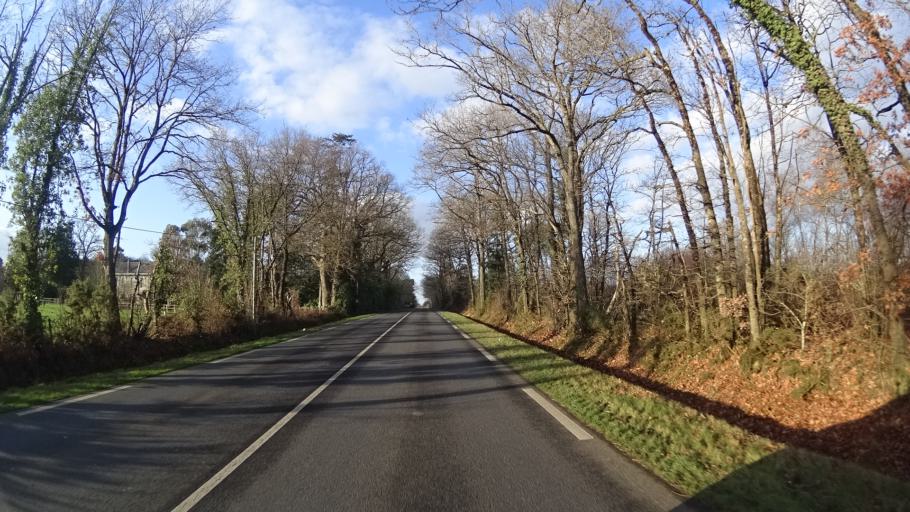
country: FR
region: Pays de la Loire
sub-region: Departement de la Loire-Atlantique
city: Saint-Nicolas-de-Redon
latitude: 47.6224
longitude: -2.0441
